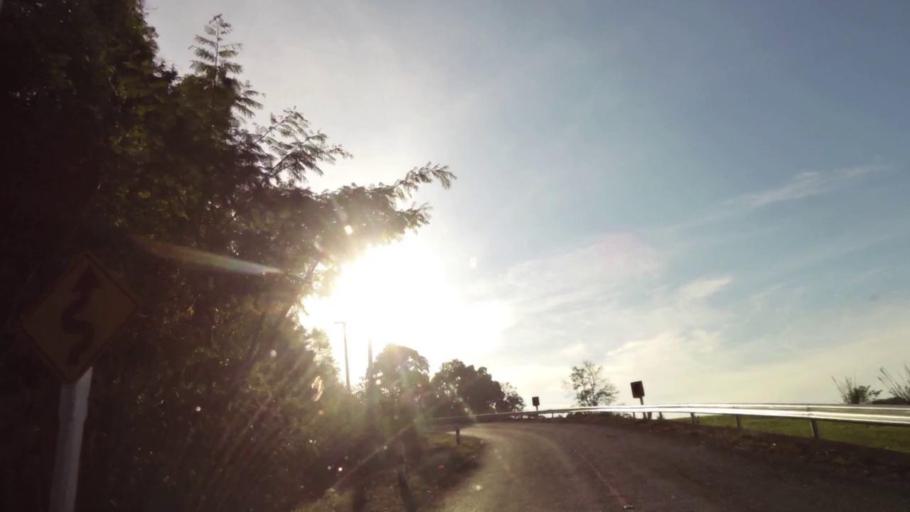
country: TH
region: Chiang Rai
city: Khun Tan
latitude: 19.8606
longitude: 100.4363
